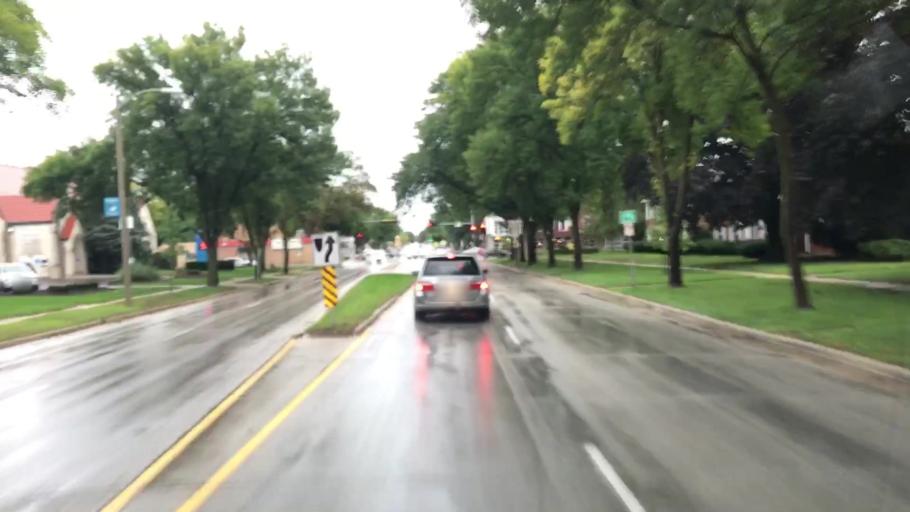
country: US
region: Wisconsin
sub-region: Milwaukee County
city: Wauwatosa
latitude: 43.0604
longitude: -88.0291
